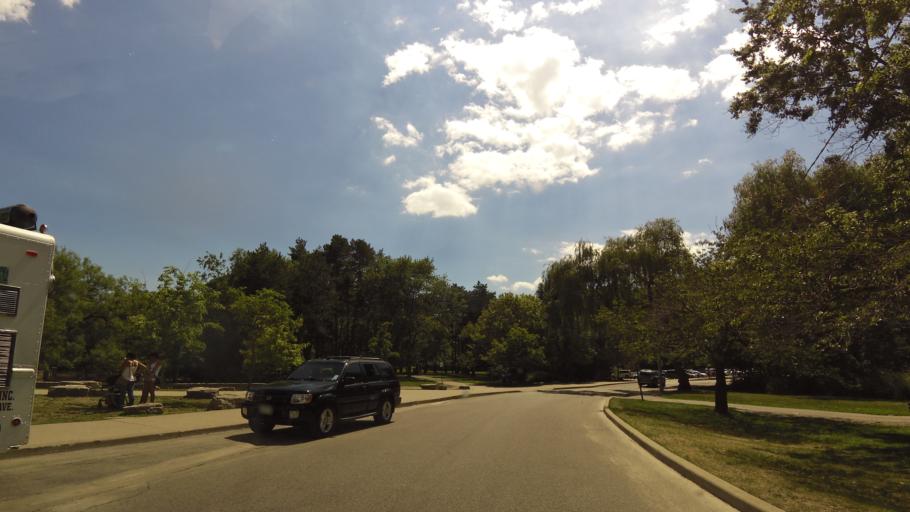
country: CA
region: Ontario
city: Toronto
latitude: 43.6435
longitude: -79.4583
